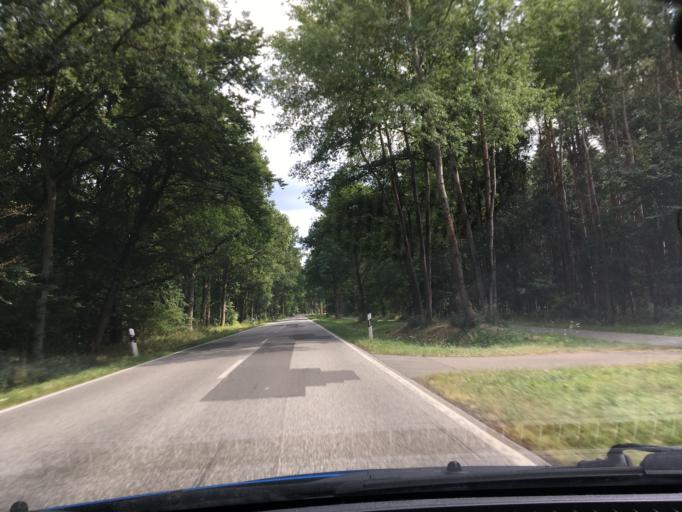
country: DE
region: Mecklenburg-Vorpommern
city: Lubtheen
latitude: 53.3566
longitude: 11.0859
